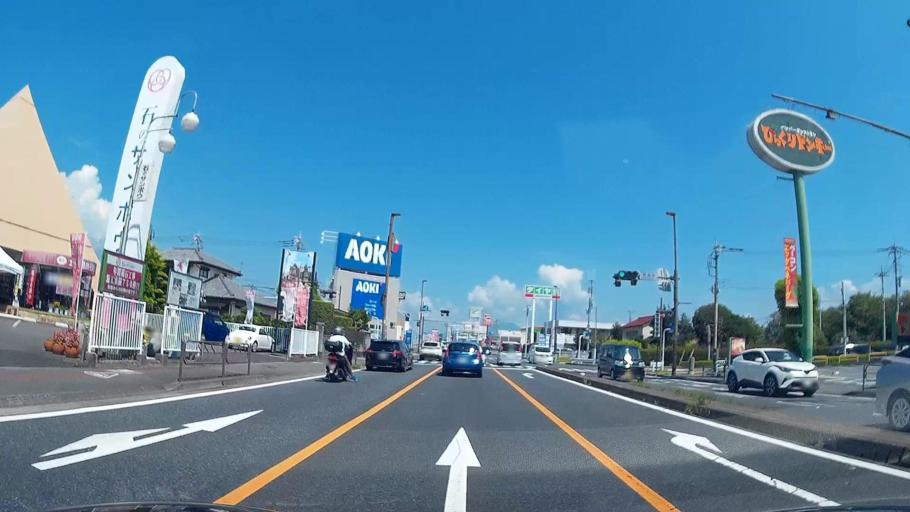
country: JP
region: Gunma
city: Maebashi-shi
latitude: 36.4228
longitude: 139.0585
